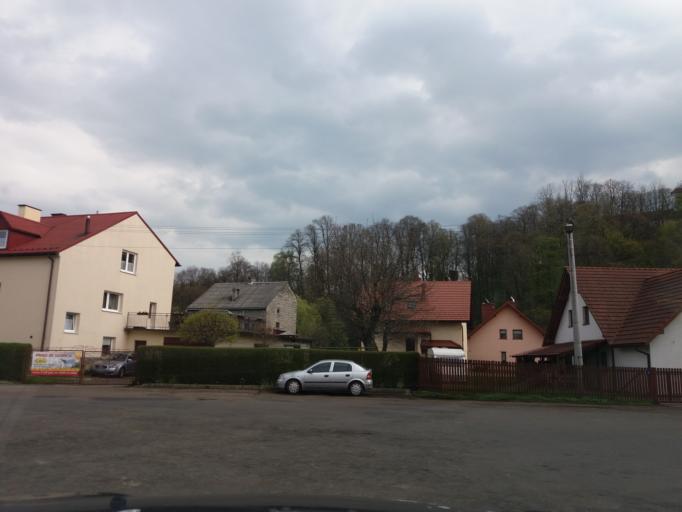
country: PL
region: Lesser Poland Voivodeship
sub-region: Powiat myslenicki
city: Dobczyce
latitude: 49.8802
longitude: 20.0868
